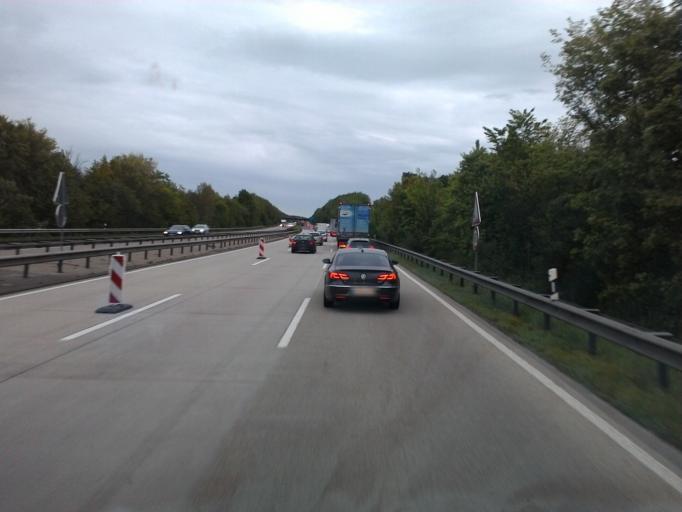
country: DE
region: Rheinland-Pfalz
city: Waldorf
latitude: 50.4798
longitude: 7.2205
